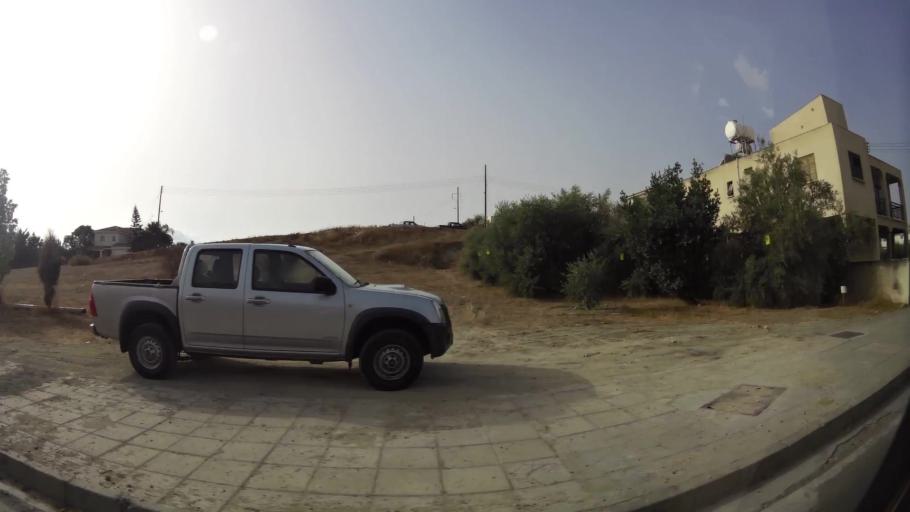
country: CY
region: Lefkosia
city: Geri
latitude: 35.0729
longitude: 33.3909
